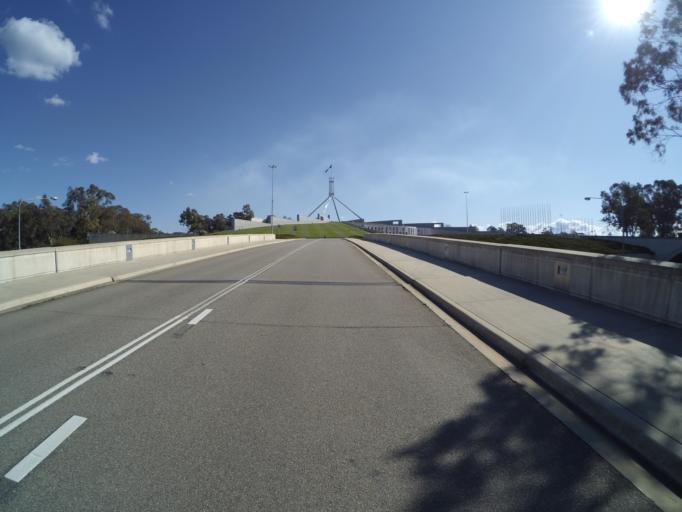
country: AU
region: Australian Capital Territory
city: Forrest
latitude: -35.3068
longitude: 149.1280
